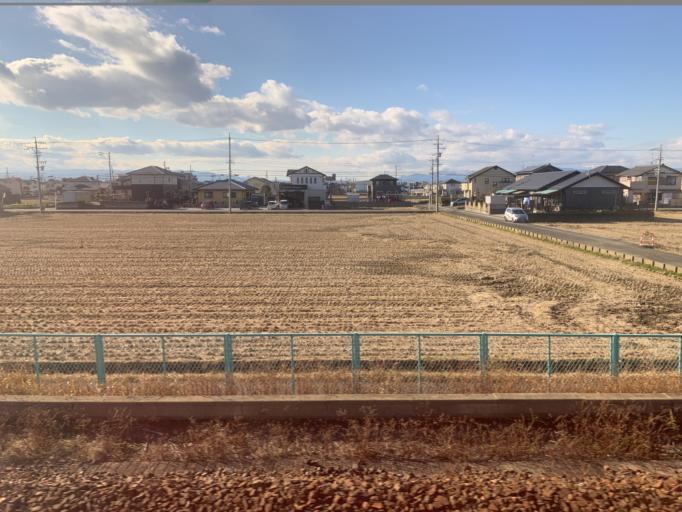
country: JP
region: Aichi
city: Kuroda
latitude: 35.3589
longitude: 136.7792
